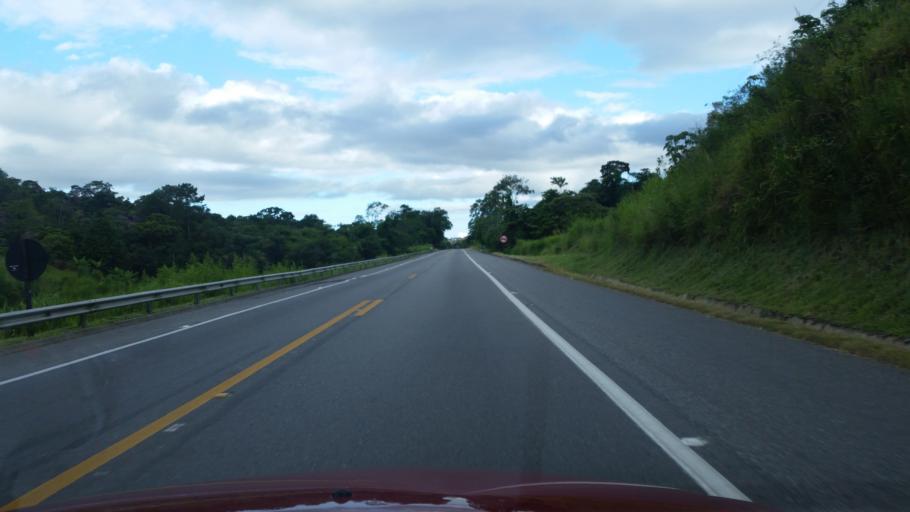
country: BR
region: Sao Paulo
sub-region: Miracatu
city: Miracatu
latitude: -24.2754
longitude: -47.2521
